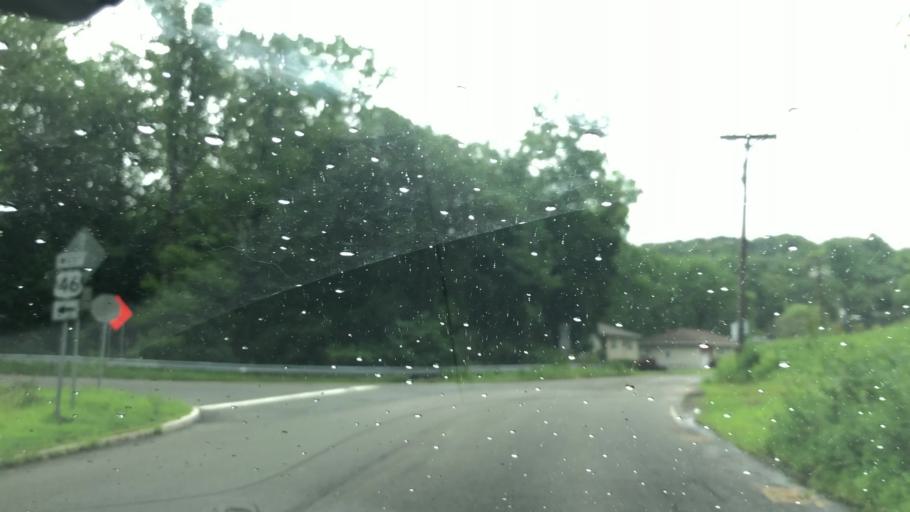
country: US
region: New Jersey
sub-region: Passaic County
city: Little Falls
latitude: 40.8790
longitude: -74.2047
